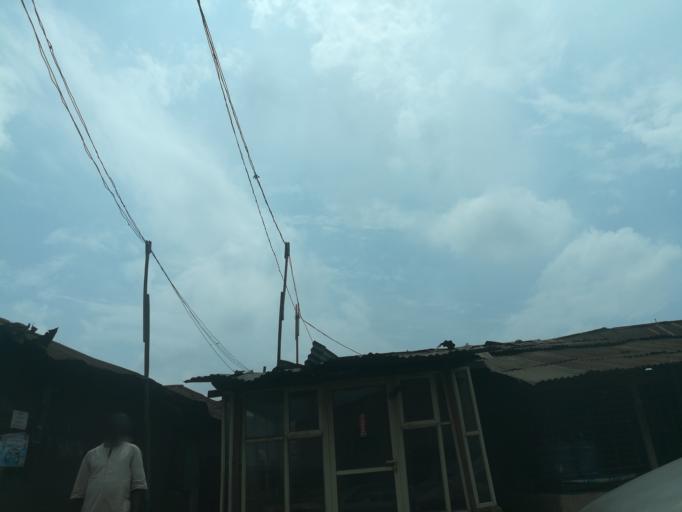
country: NG
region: Lagos
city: Ikorodu
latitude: 6.6113
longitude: 3.5052
